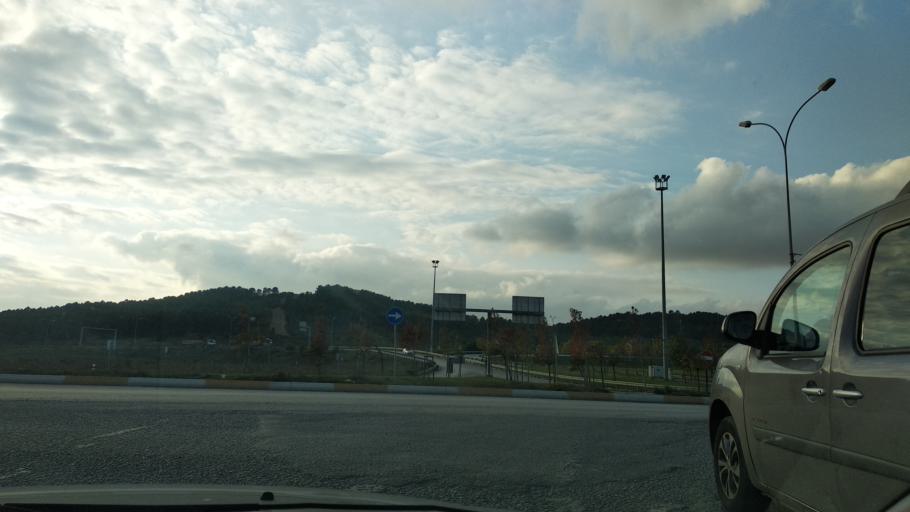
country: TR
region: Istanbul
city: Icmeler
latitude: 40.9203
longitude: 29.3426
